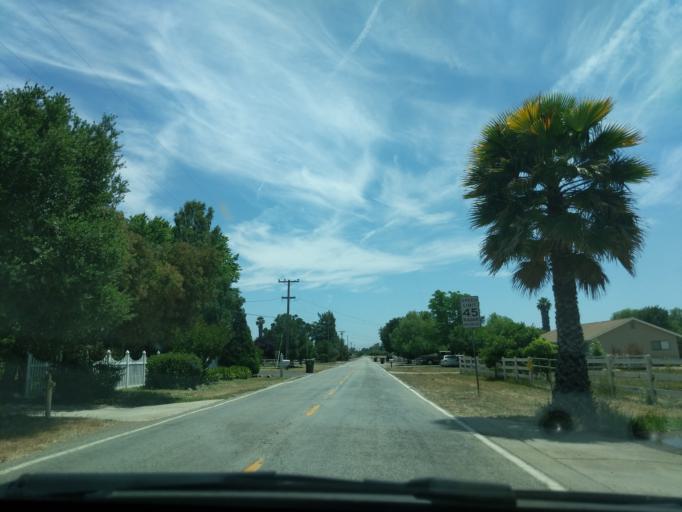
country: US
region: California
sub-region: Santa Clara County
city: San Martin
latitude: 37.0580
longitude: -121.5675
